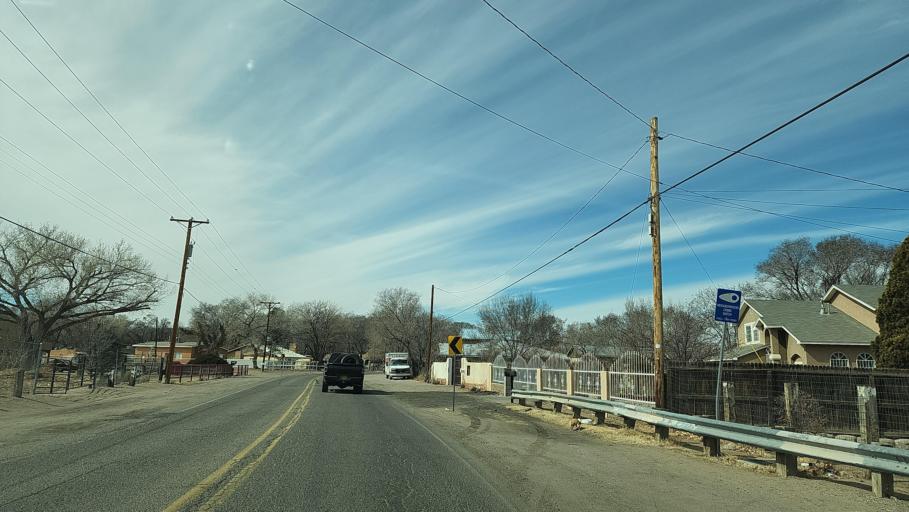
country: US
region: New Mexico
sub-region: Bernalillo County
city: South Valley
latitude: 35.0362
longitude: -106.7017
